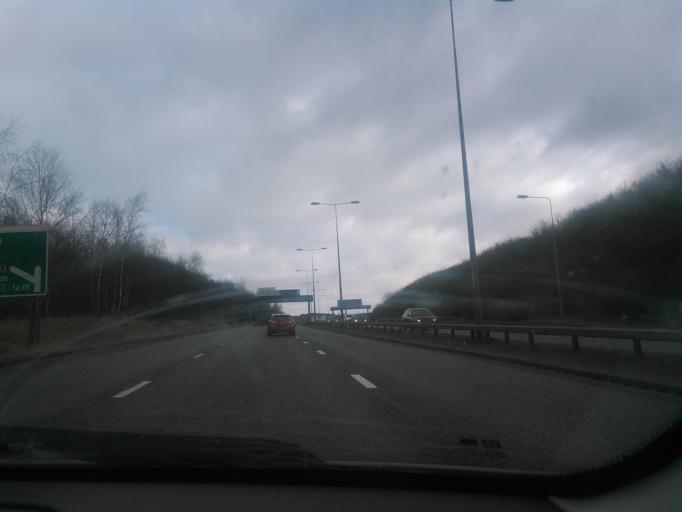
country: GB
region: England
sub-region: Staffordshire
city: Longton
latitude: 52.9914
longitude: -2.1537
